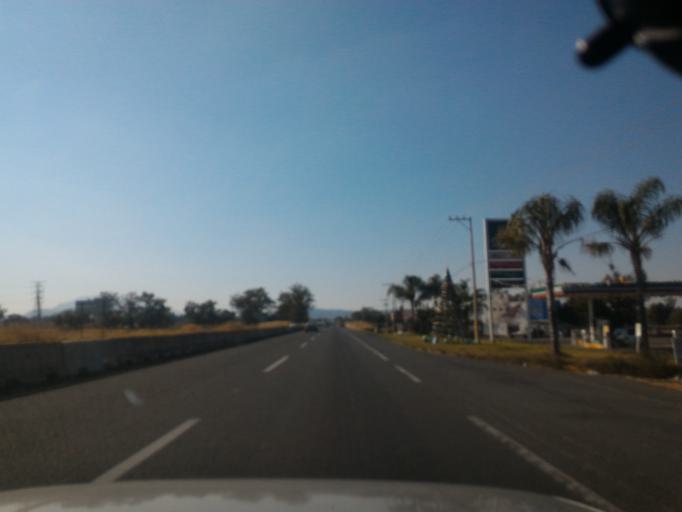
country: MX
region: Jalisco
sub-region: Ixtlahuacan de los Membrillos
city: Valle de los Girasoles [Fraccionamiento]
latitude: 20.4033
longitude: -103.1738
